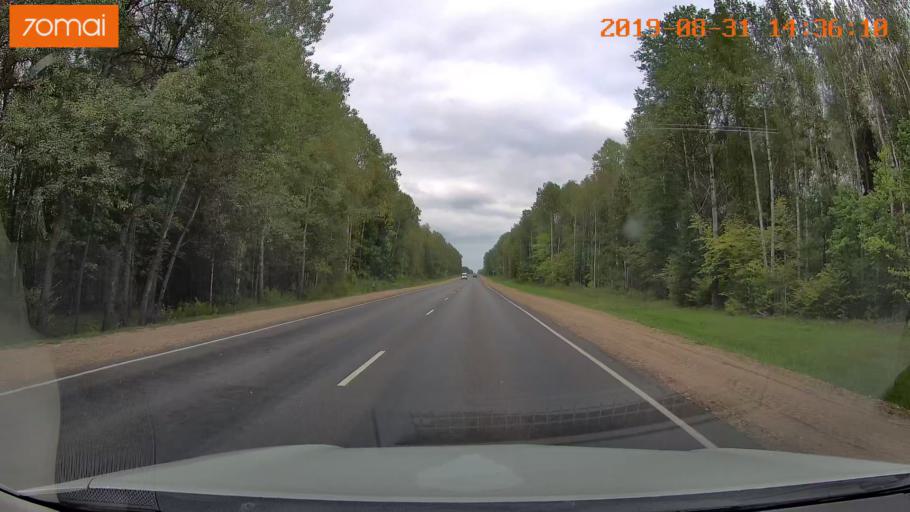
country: RU
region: Smolensk
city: Yekimovichi
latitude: 54.1681
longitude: 33.4734
